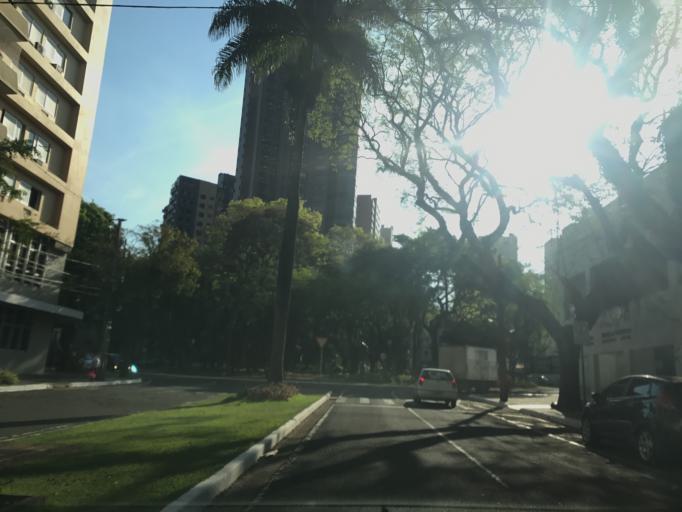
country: BR
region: Parana
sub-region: Maringa
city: Maringa
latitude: -23.4236
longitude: -51.9446
